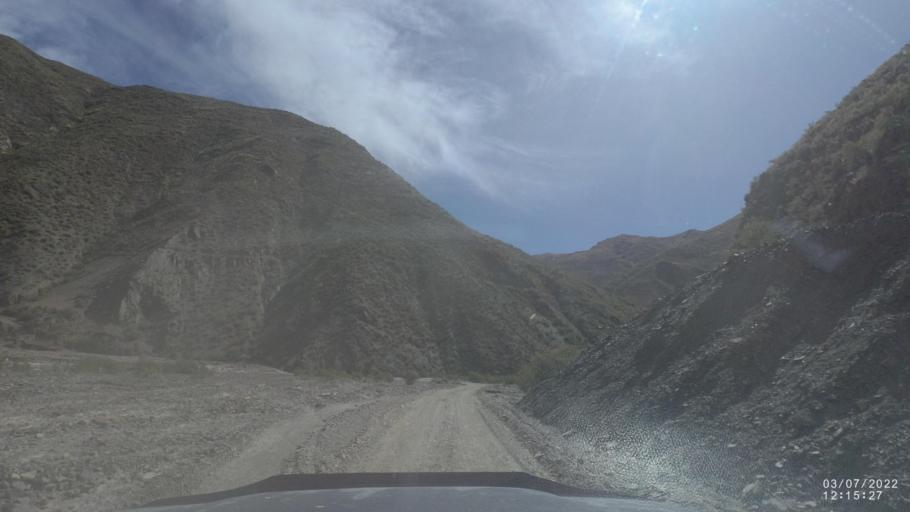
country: BO
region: Cochabamba
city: Irpa Irpa
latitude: -17.8292
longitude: -66.6070
